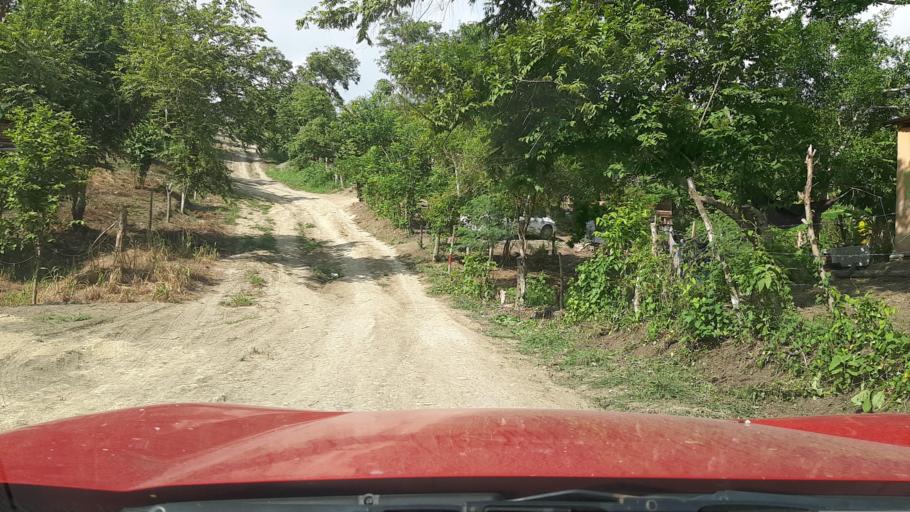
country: MX
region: Veracruz
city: Coatzintla
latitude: 20.5035
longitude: -97.4601
